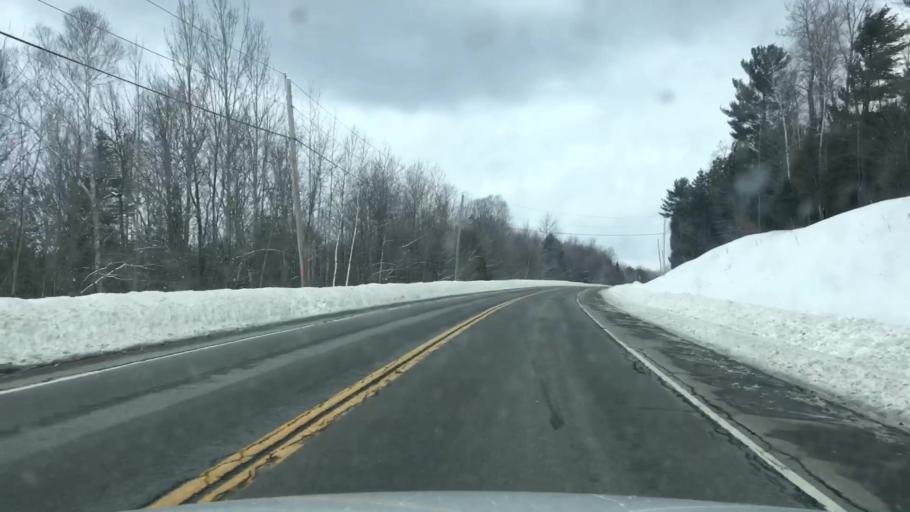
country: US
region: Maine
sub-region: Somerset County
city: Cornville
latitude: 44.8115
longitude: -69.7066
